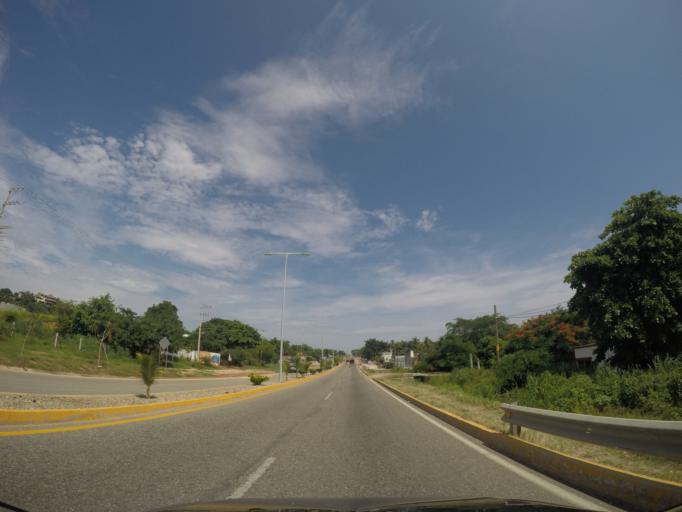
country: MX
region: Oaxaca
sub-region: Santa Maria Colotepec
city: Brisas de Zicatela
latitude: 15.8434
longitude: -97.0445
